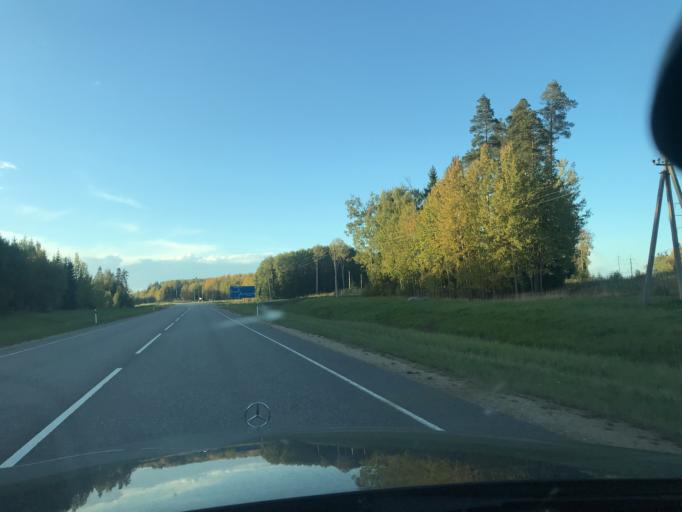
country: EE
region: Vorumaa
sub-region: Voru linn
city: Voru
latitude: 57.8464
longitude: 27.0435
